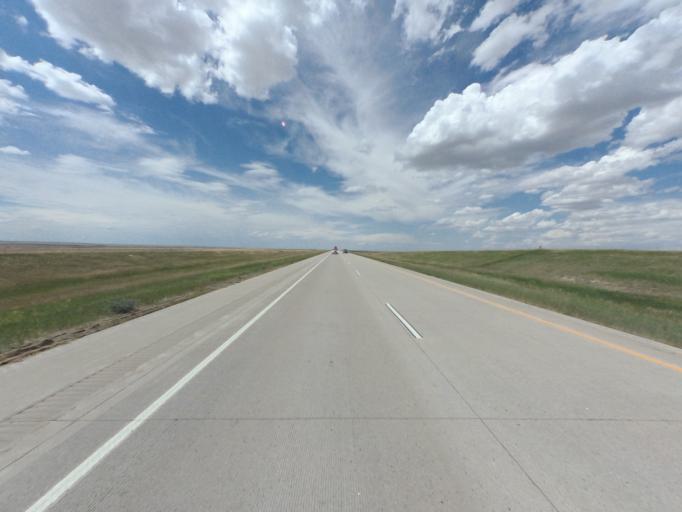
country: US
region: Colorado
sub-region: Lincoln County
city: Limon
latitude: 39.4029
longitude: -103.9004
